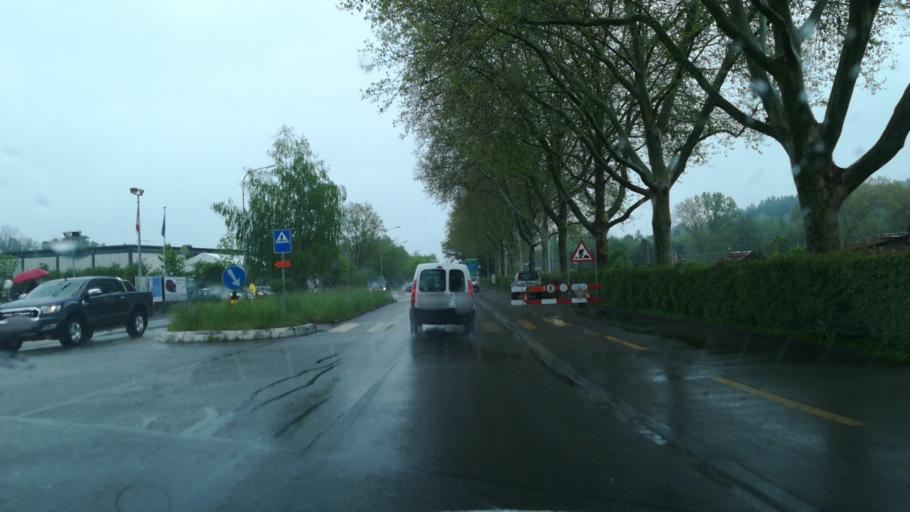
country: CH
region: Zurich
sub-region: Bezirk Winterthur
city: Veltheim
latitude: 47.5199
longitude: 8.7182
